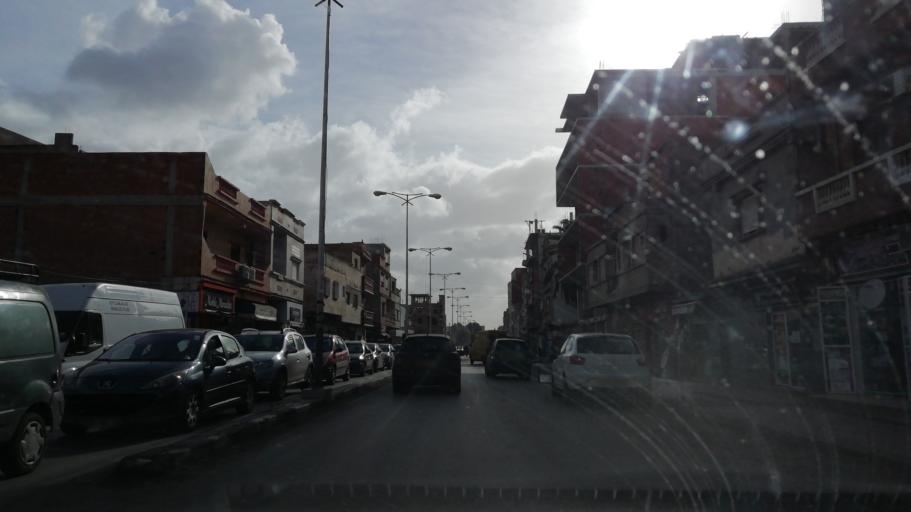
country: DZ
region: Oran
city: Oran
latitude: 35.6870
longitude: -0.6236
